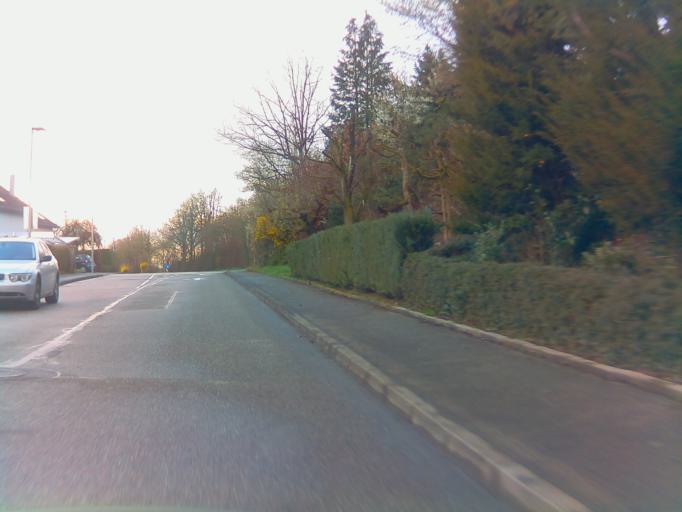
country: DE
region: Baden-Wuerttemberg
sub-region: Regierungsbezirk Stuttgart
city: Untergruppenbach
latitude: 49.1045
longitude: 9.2867
